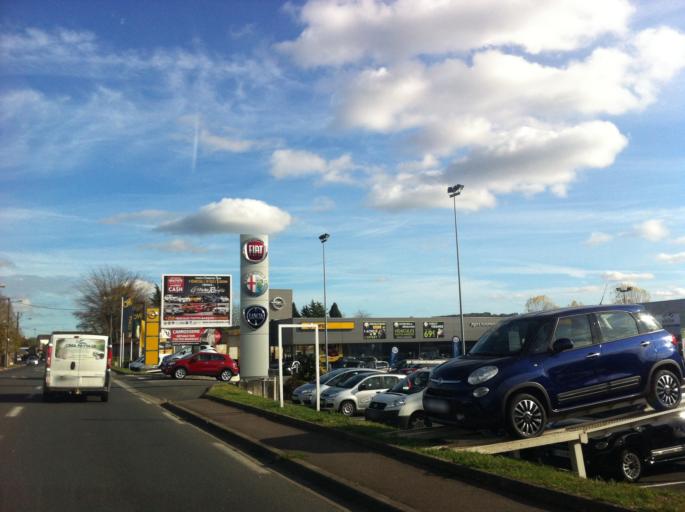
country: FR
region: Aquitaine
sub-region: Departement de la Dordogne
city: Perigueux
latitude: 45.1900
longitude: 0.7449
